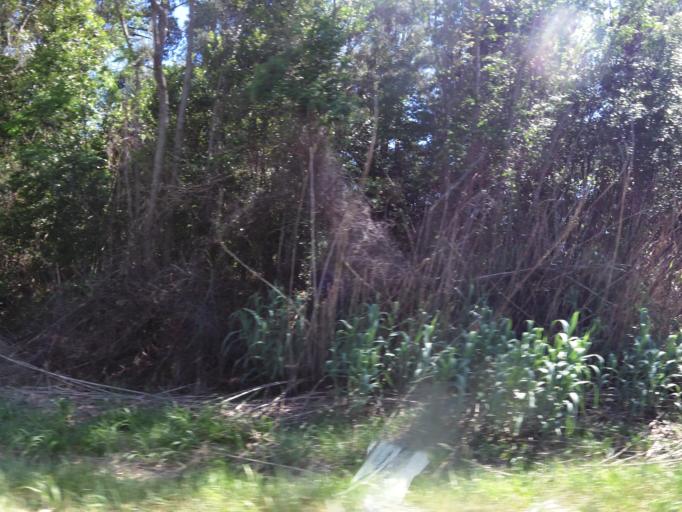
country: US
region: South Carolina
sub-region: Aiken County
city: New Ellenton
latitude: 33.5175
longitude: -81.5912
